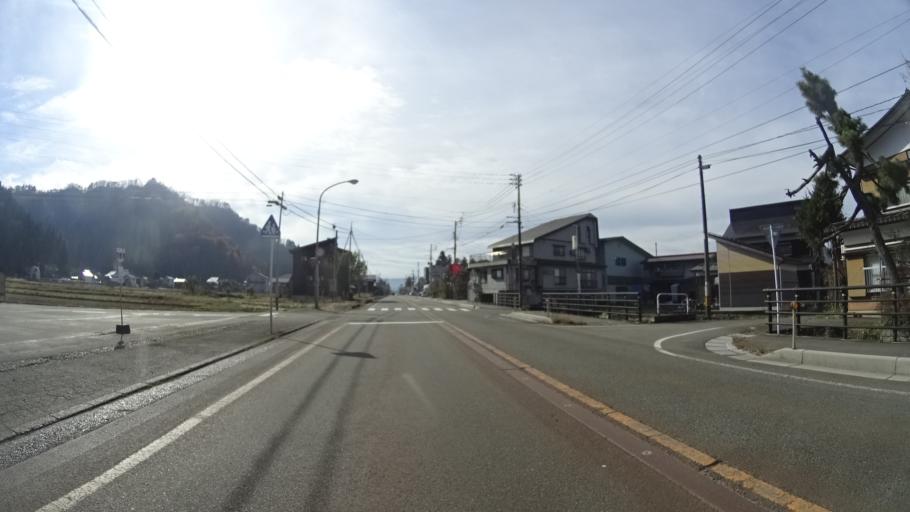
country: JP
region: Niigata
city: Muikamachi
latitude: 37.1238
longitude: 138.9293
